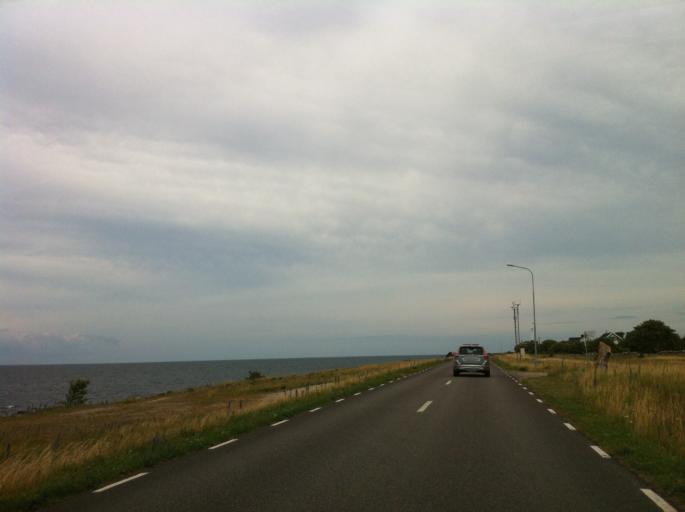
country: SE
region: Kalmar
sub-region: Vasterviks Kommun
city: Vaestervik
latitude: 57.3380
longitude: 17.0147
